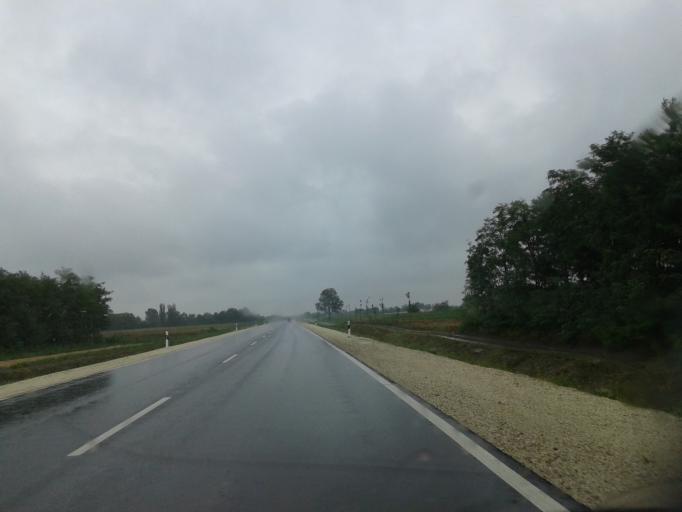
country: HU
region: Csongrad
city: Morahalom
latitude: 46.2278
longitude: 19.8394
